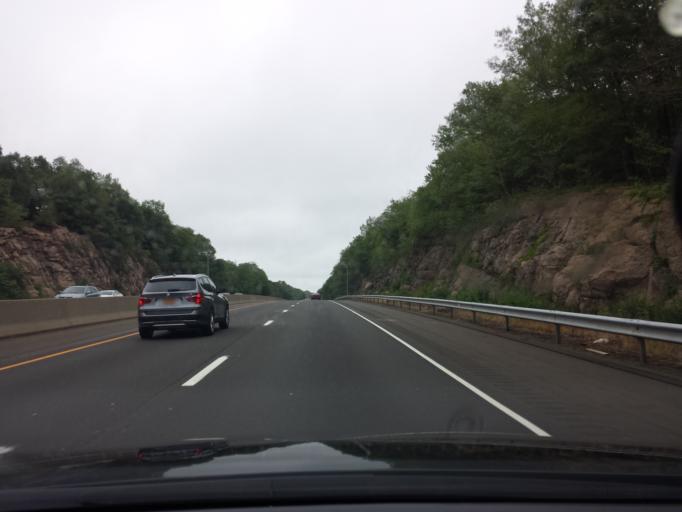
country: US
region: Connecticut
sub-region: New Haven County
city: North Branford
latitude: 41.2971
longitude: -72.7396
